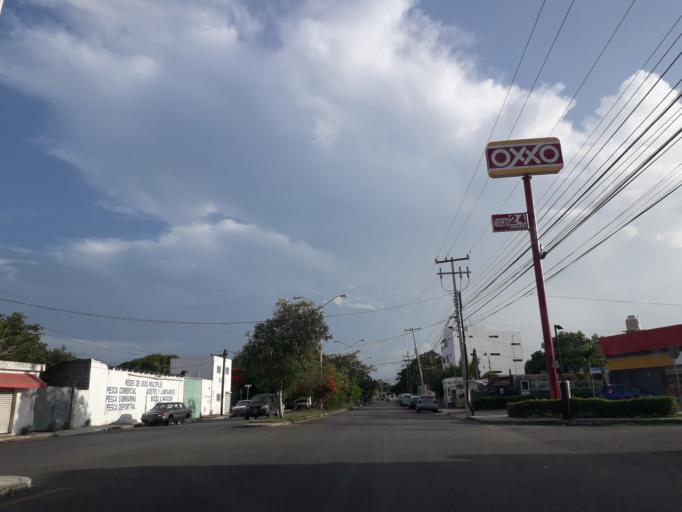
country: MX
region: Yucatan
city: Merida
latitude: 21.0233
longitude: -89.6306
